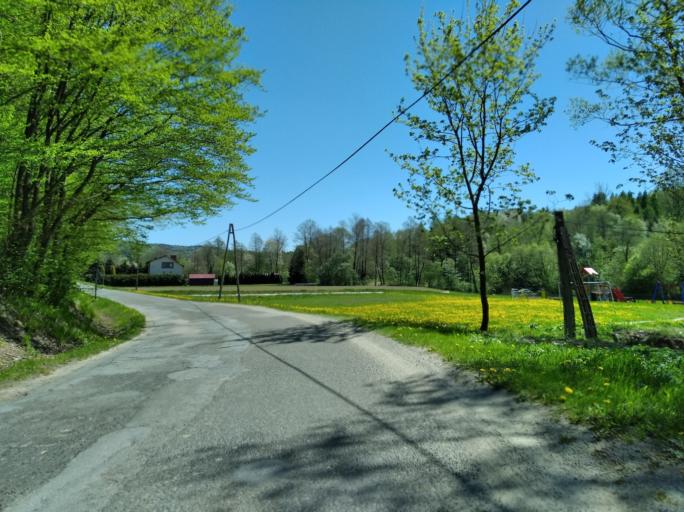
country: PL
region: Subcarpathian Voivodeship
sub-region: Powiat debicki
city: Brzostek
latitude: 49.9111
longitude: 21.4720
